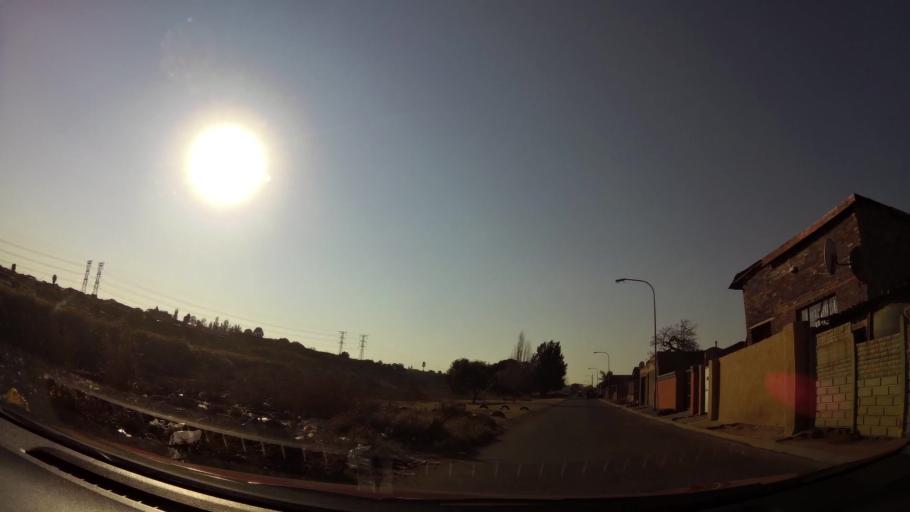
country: ZA
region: Gauteng
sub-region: City of Johannesburg Metropolitan Municipality
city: Soweto
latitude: -26.2562
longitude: 27.9461
